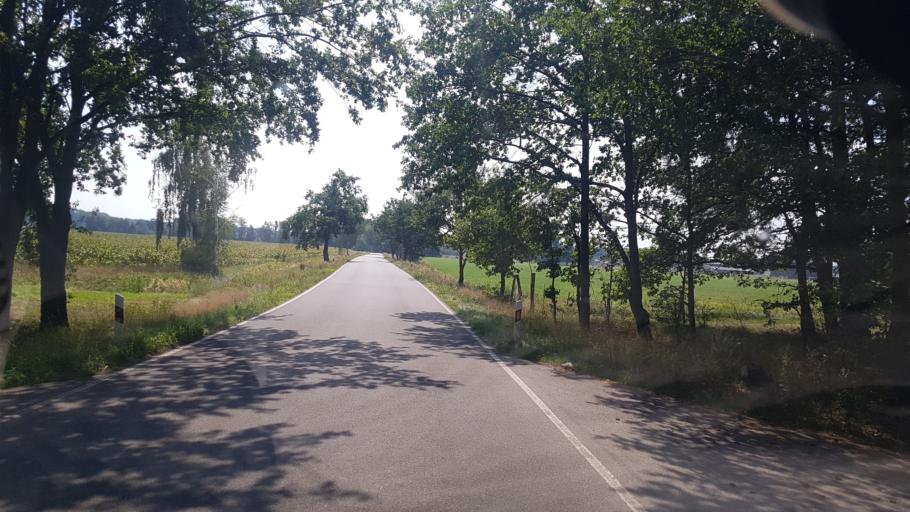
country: DE
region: Brandenburg
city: Cottbus
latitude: 51.7047
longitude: 14.4261
